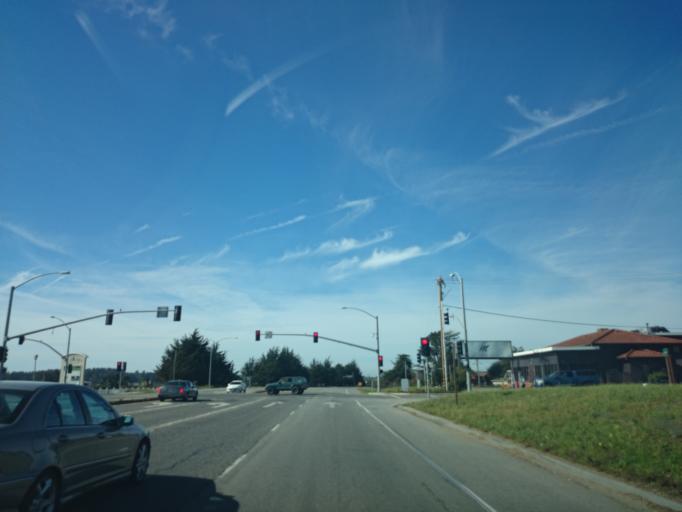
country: US
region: California
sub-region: San Mateo County
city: El Granada
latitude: 37.5051
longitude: -122.4805
